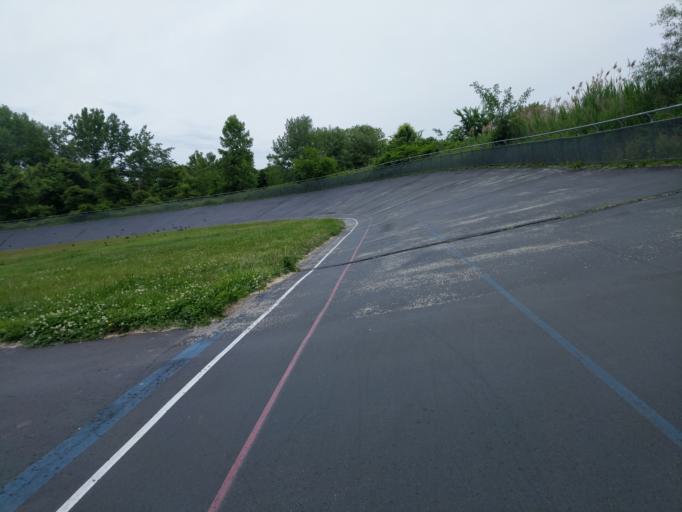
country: US
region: New York
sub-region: Queens County
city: Jamaica
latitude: 40.7444
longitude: -73.8092
